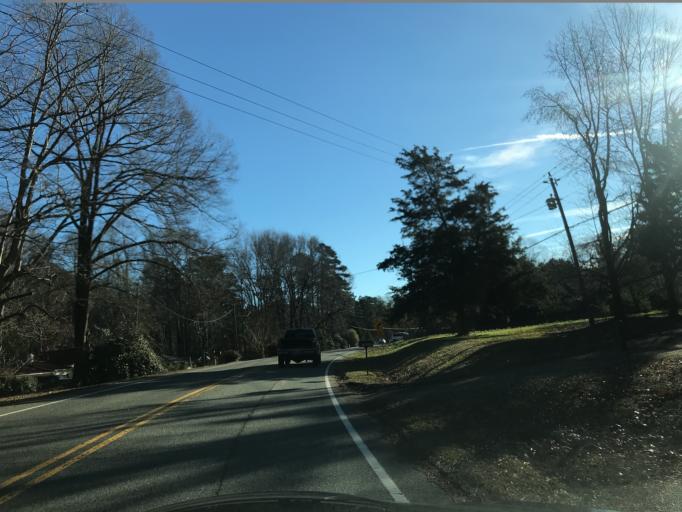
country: US
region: North Carolina
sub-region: Wake County
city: West Raleigh
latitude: 35.9089
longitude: -78.7090
